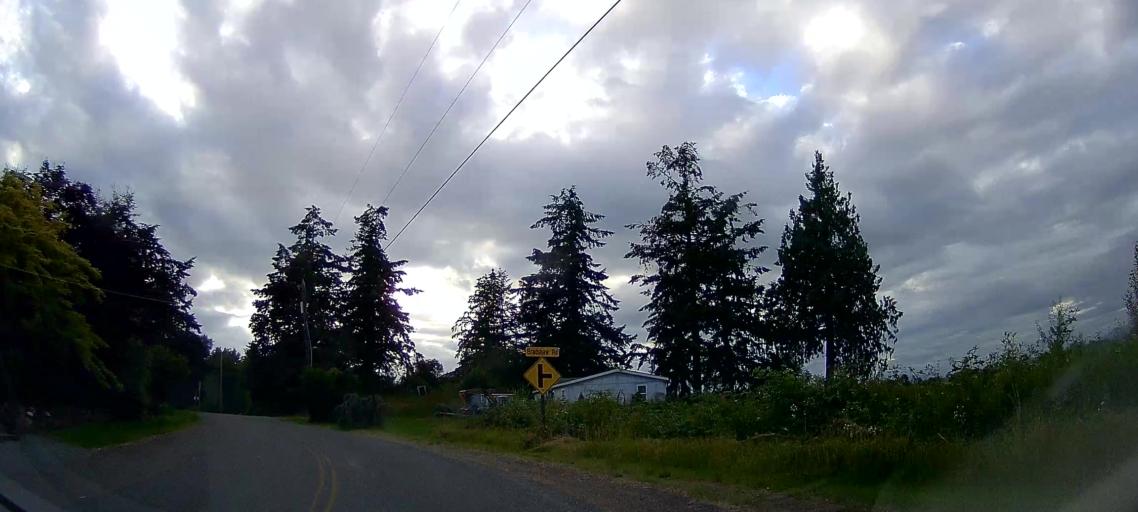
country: US
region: Washington
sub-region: Skagit County
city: Mount Vernon
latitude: 48.3659
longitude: -122.4178
